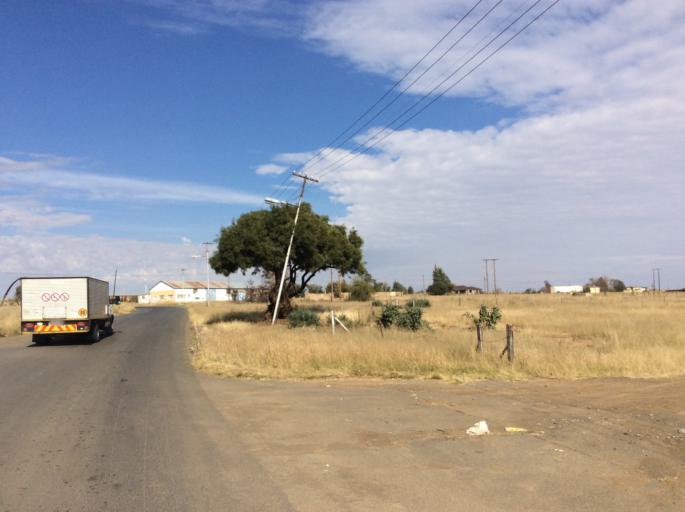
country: LS
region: Mafeteng
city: Mafeteng
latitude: -29.7334
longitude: 27.0308
